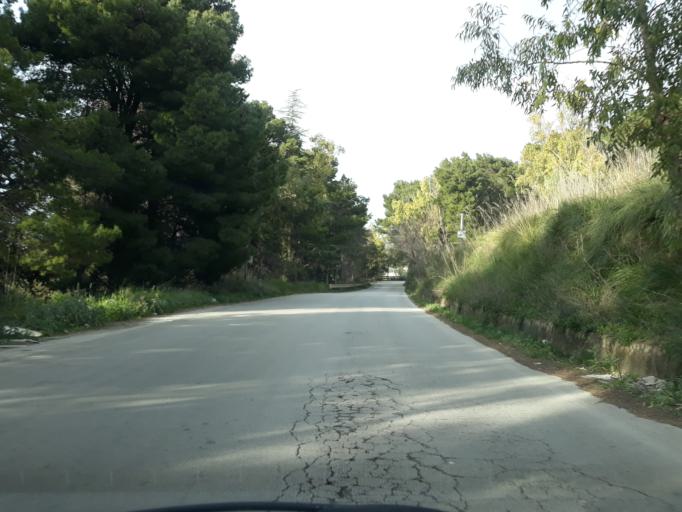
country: IT
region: Sicily
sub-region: Palermo
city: Torretta
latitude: 38.1108
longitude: 13.2383
